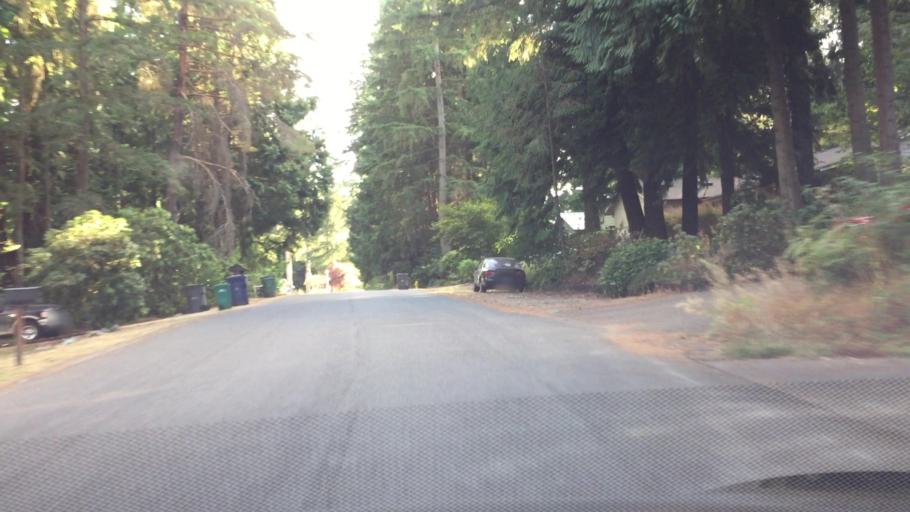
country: US
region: Washington
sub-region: King County
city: Cottage Lake
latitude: 47.7565
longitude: -122.0939
